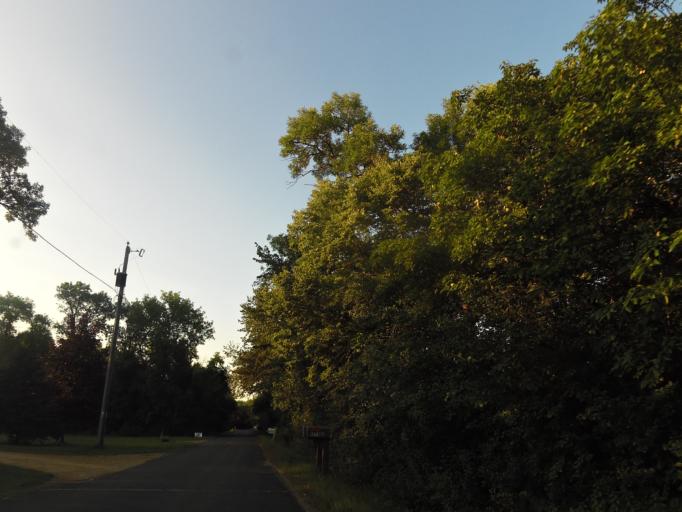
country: US
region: Minnesota
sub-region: Washington County
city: Stillwater
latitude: 45.0617
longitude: -92.7890
